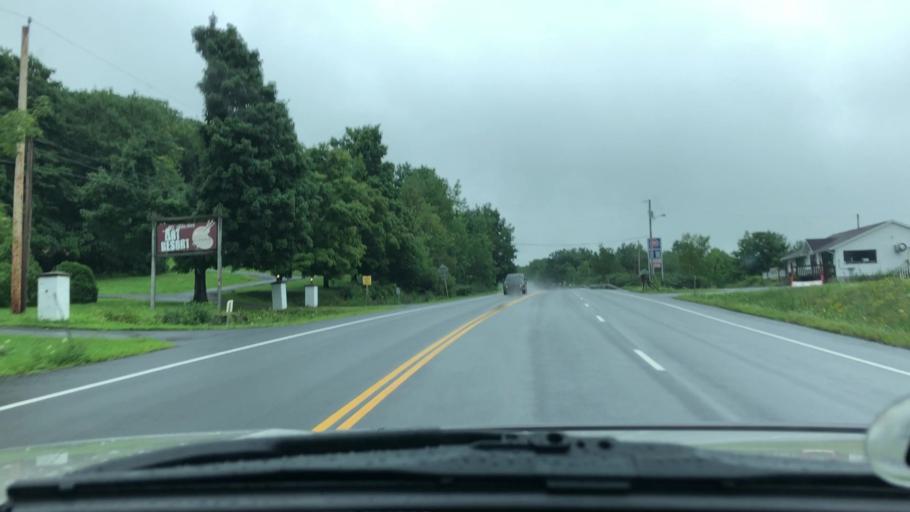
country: US
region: New York
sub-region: Greene County
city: Cairo
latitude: 42.3297
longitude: -74.1135
